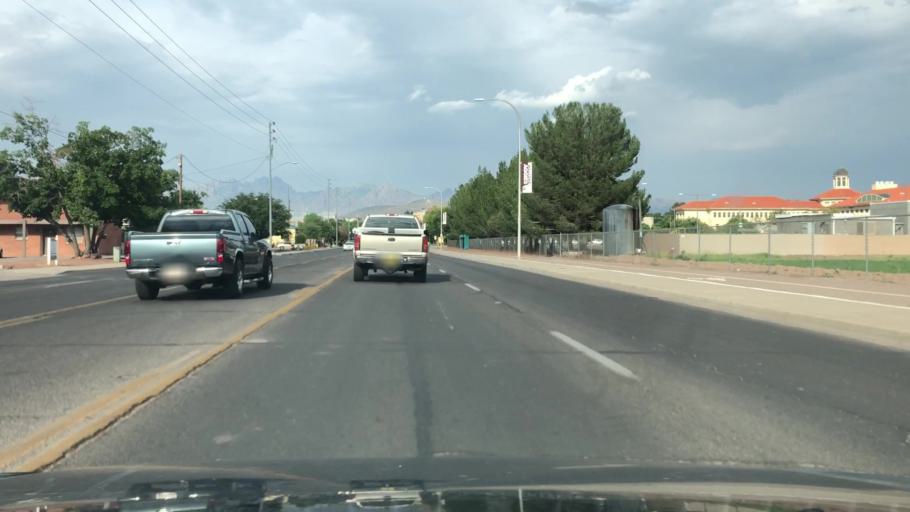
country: US
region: New Mexico
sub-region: Dona Ana County
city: University Park
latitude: 32.2832
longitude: -106.7605
